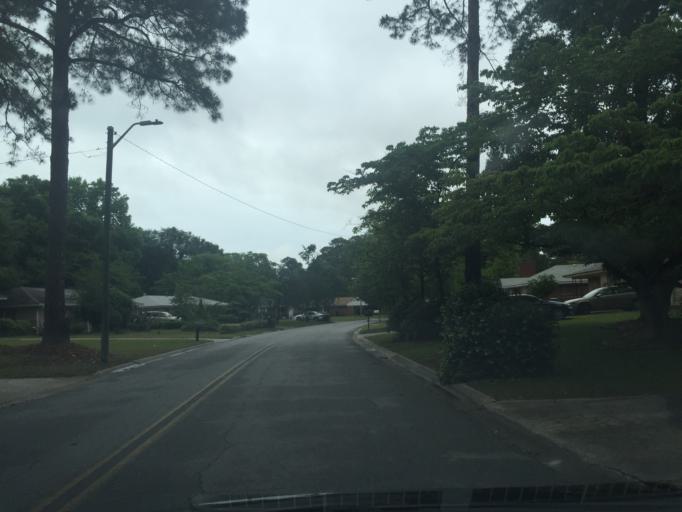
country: US
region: Georgia
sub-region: Chatham County
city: Montgomery
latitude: 31.9869
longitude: -81.1255
